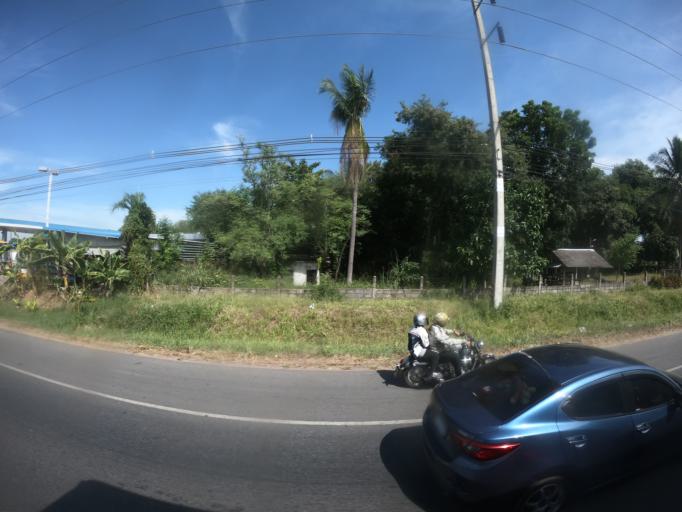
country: TH
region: Maha Sarakham
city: Chiang Yuen
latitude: 16.4419
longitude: 102.9763
